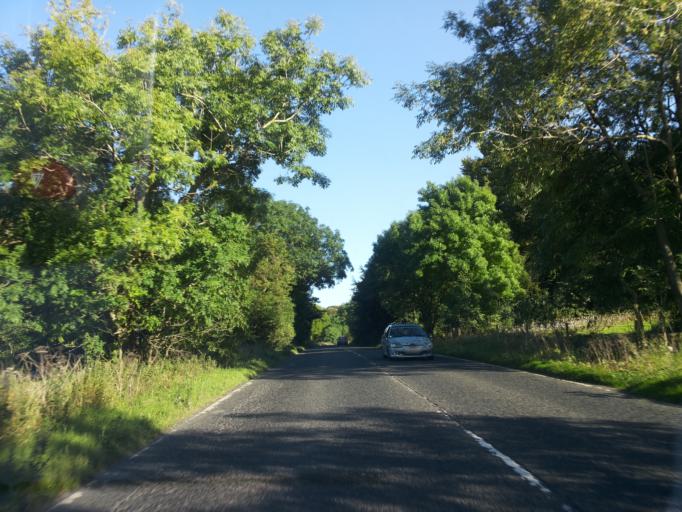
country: GB
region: England
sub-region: Derbyshire
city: Tideswell
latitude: 53.2414
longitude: -1.8140
